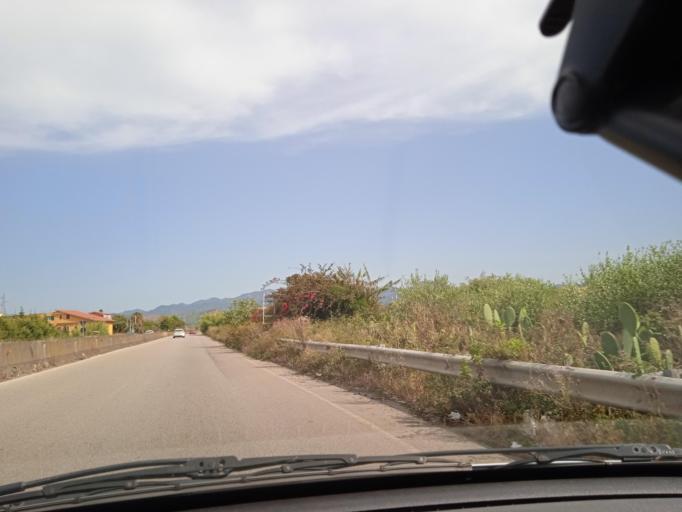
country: IT
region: Sicily
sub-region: Messina
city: Milazzo
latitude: 38.1950
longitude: 15.2561
